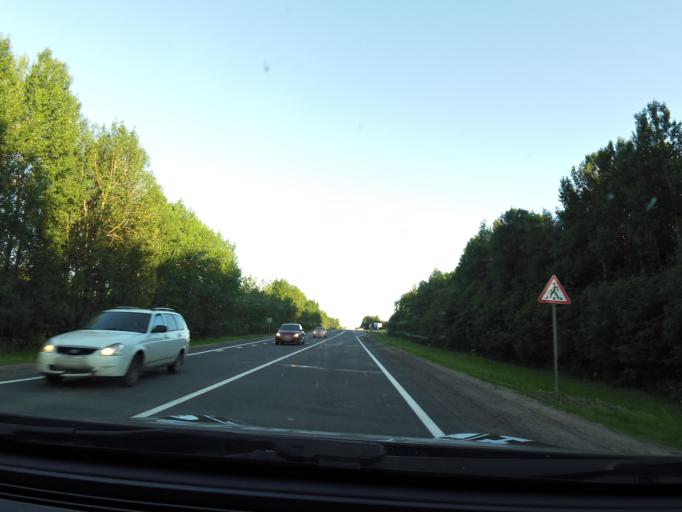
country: RU
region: Vologda
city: Gryazovets
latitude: 58.7877
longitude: 40.2695
